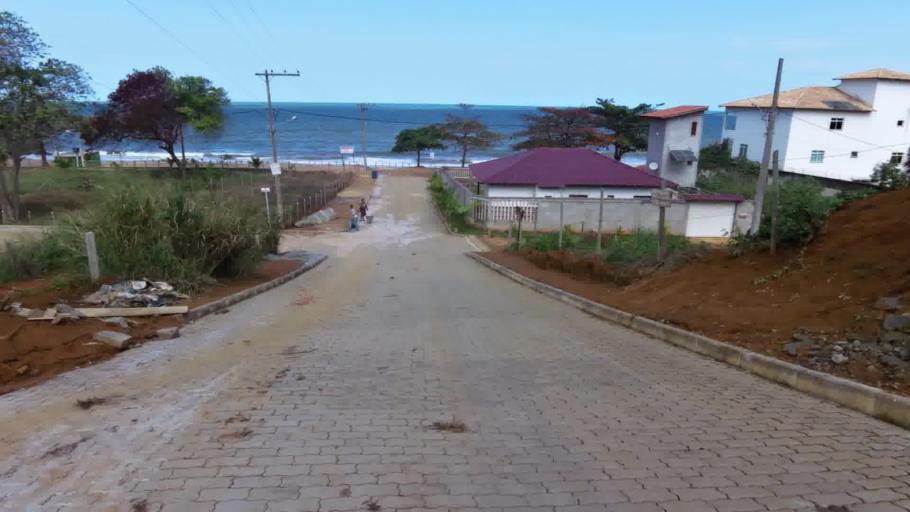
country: BR
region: Espirito Santo
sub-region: Piuma
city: Piuma
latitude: -20.8260
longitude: -40.6871
